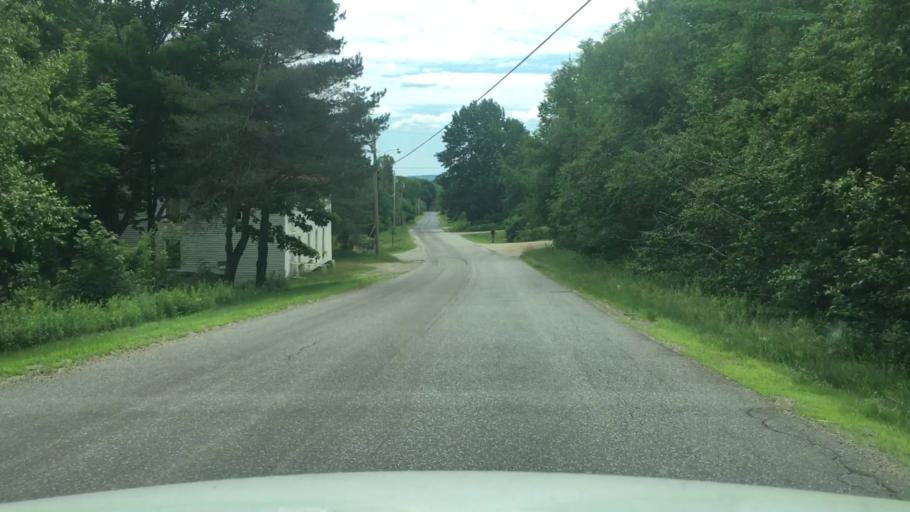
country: US
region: Maine
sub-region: Waldo County
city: Searsmont
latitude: 44.4471
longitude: -69.2469
